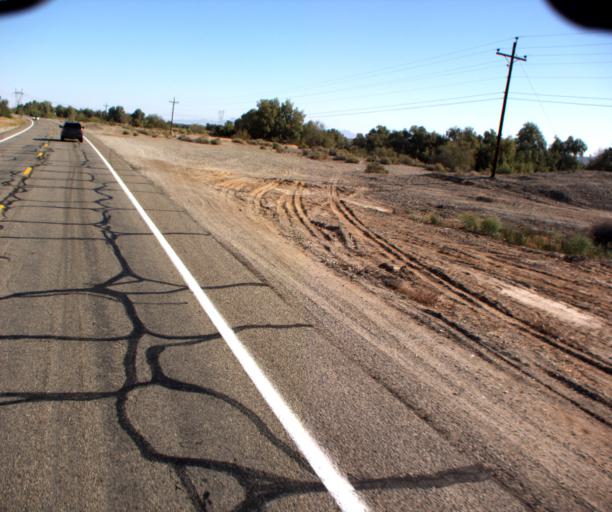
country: US
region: Arizona
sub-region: Yuma County
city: Fortuna Foothills
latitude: 32.7807
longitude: -114.3828
